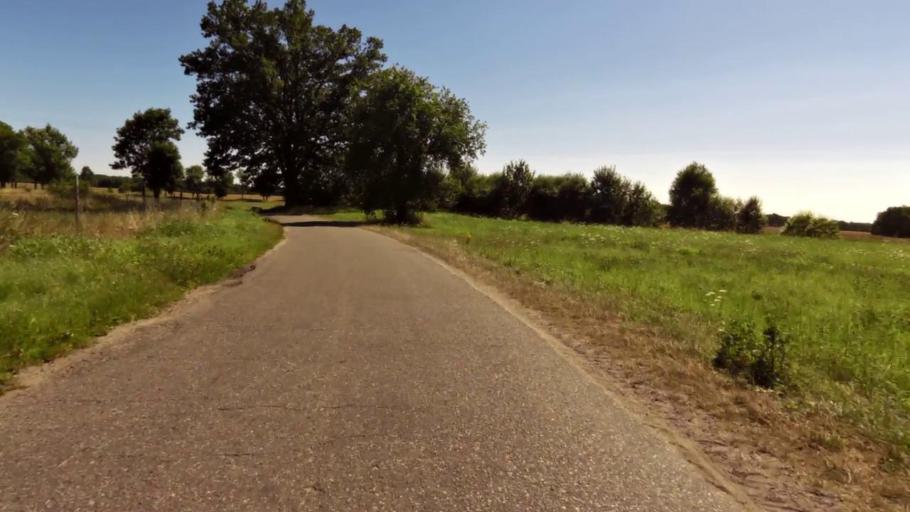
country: PL
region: West Pomeranian Voivodeship
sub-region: Powiat szczecinecki
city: Szczecinek
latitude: 53.6825
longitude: 16.5950
